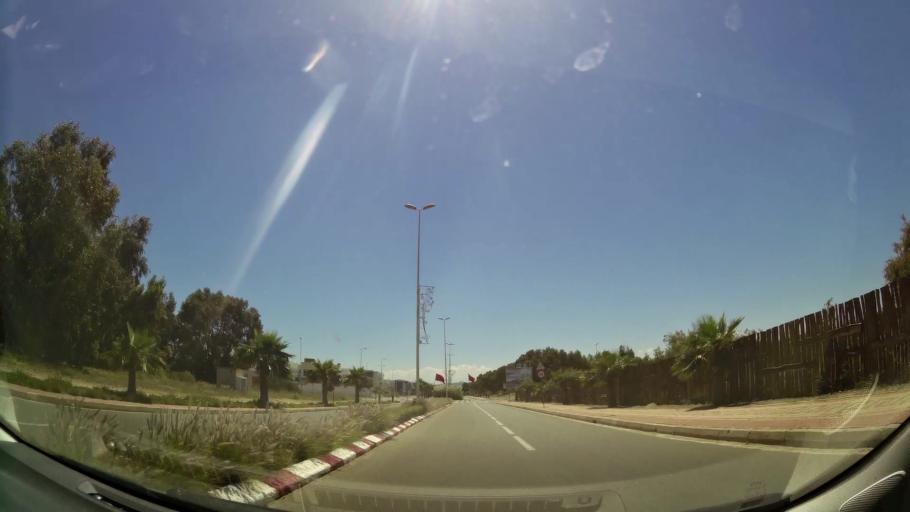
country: MA
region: Oriental
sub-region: Berkane-Taourirt
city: Madagh
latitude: 35.0936
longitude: -2.2669
